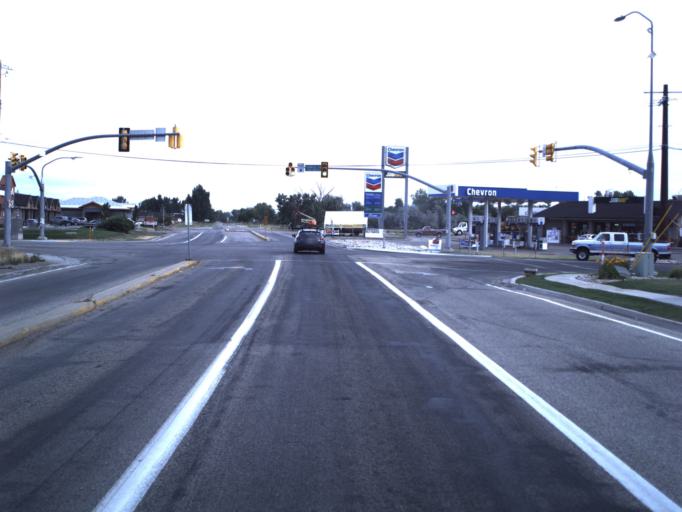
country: US
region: Utah
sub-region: Weber County
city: Marriott-Slaterville
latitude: 41.2692
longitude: -112.0282
